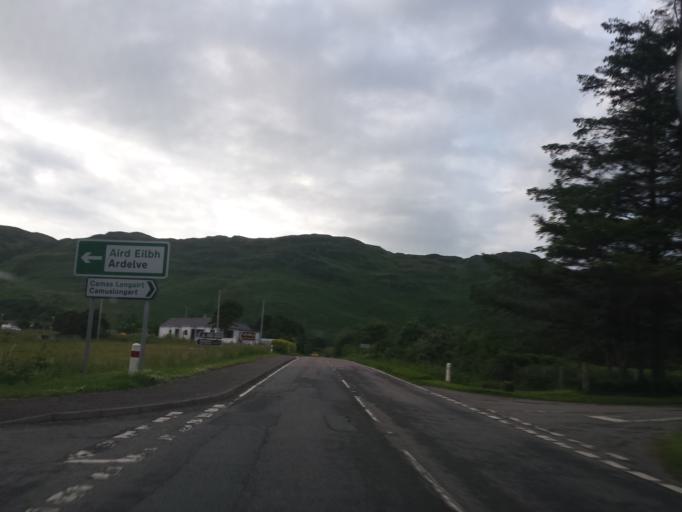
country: GB
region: Scotland
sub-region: Highland
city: Fort William
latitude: 57.2809
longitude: -5.5226
